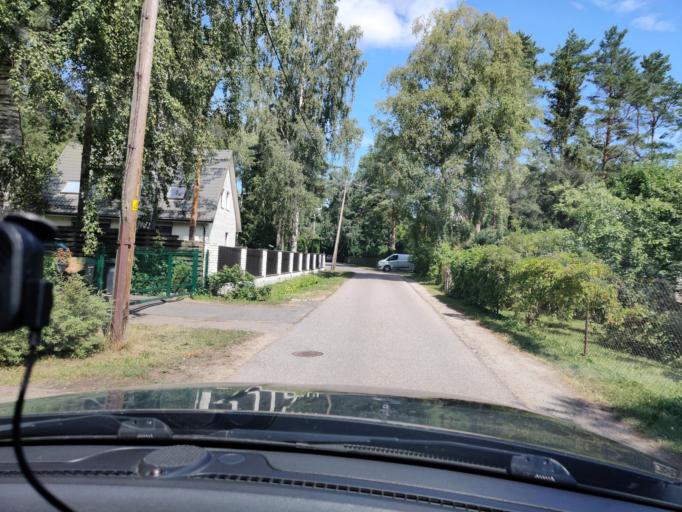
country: EE
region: Harju
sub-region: Saue vald
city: Laagri
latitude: 59.3769
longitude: 24.6393
